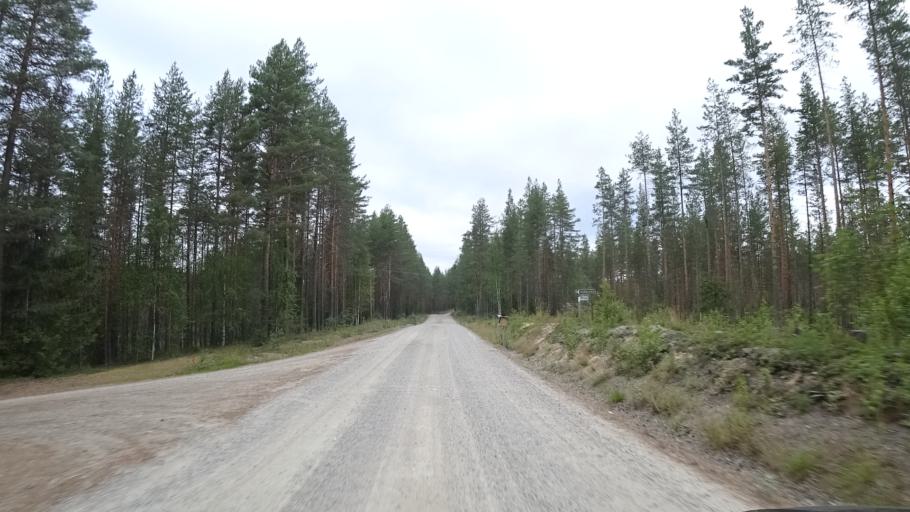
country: FI
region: North Karelia
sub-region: Pielisen Karjala
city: Lieksa
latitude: 63.2462
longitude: 30.3398
